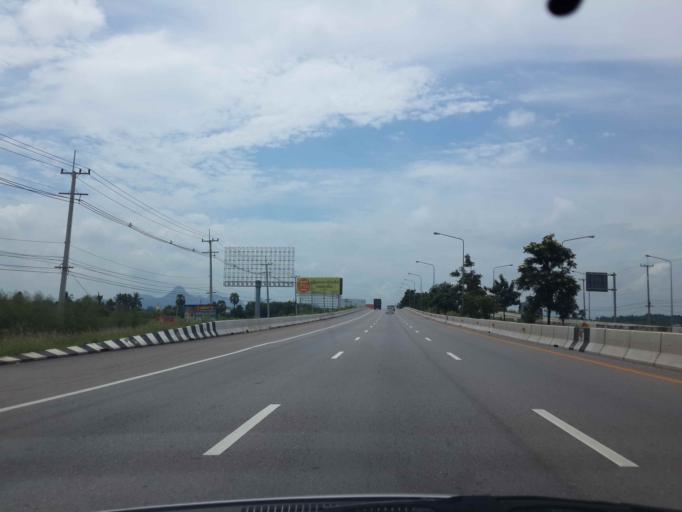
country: TH
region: Ratchaburi
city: Pak Tho
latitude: 13.3416
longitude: 99.8513
